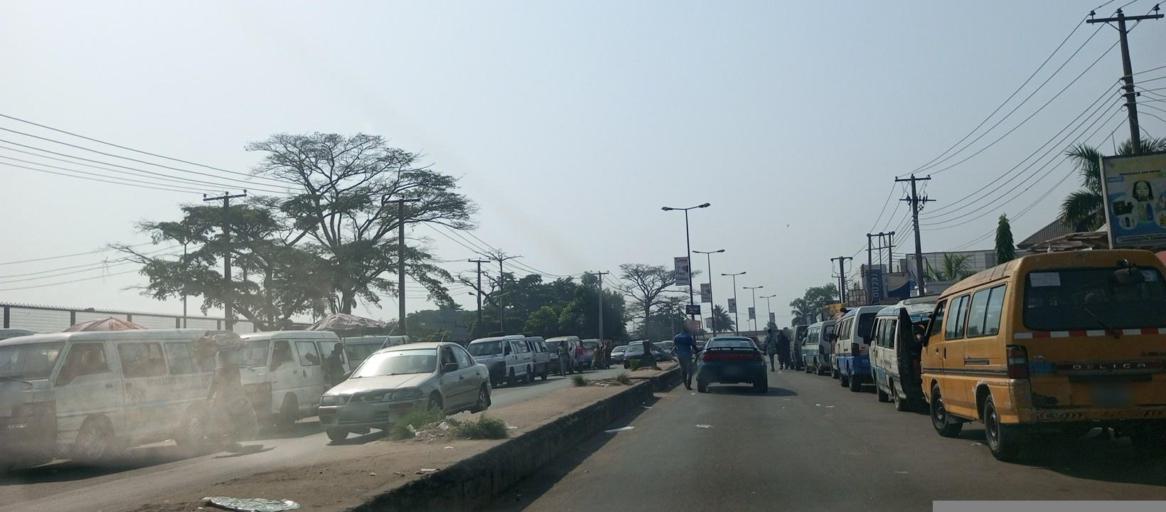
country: NG
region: Rivers
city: Emuoha
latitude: 4.8970
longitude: 6.9069
